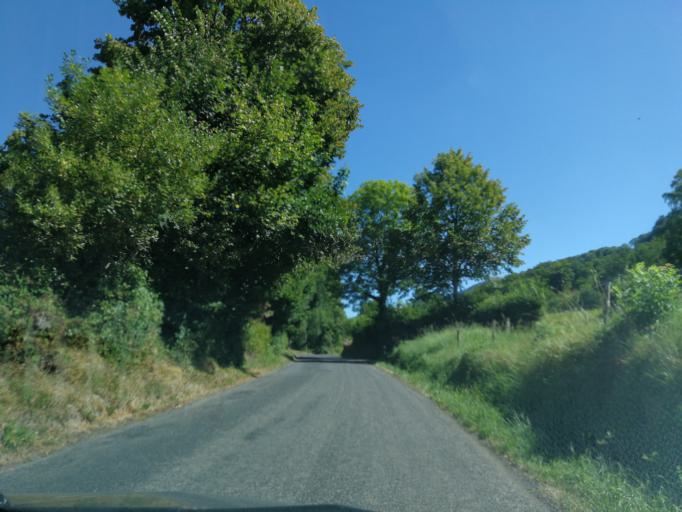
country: FR
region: Auvergne
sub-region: Departement du Cantal
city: Vic-sur-Cere
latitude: 45.0294
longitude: 2.5832
